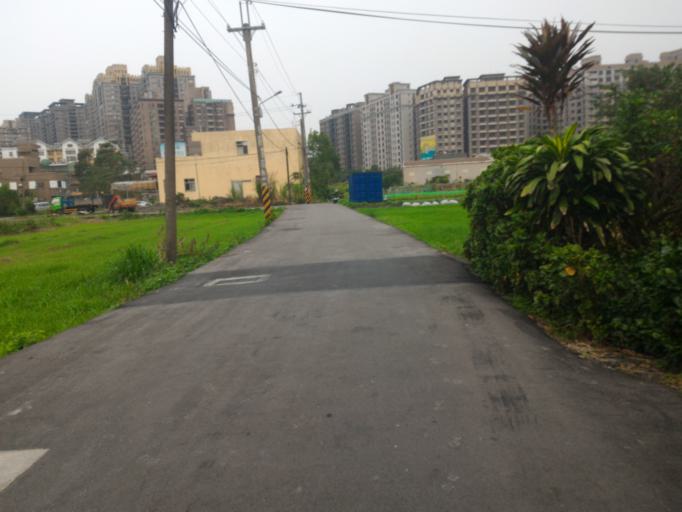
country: TW
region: Taiwan
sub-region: Taoyuan
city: Taoyuan
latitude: 24.9478
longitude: 121.3876
